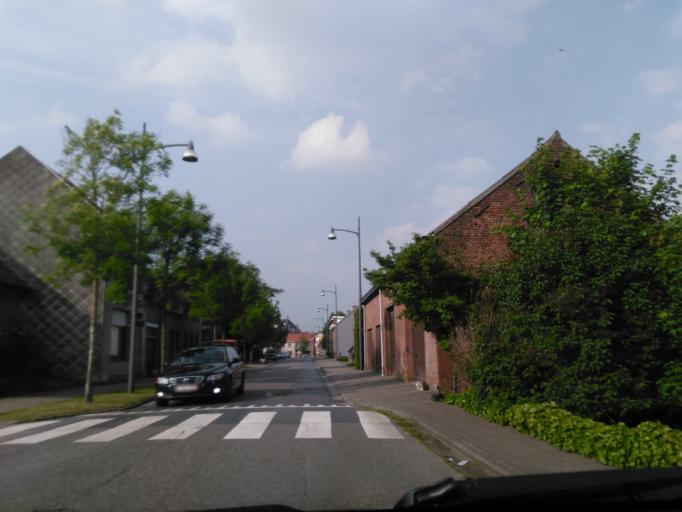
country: BE
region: Flanders
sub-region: Provincie Oost-Vlaanderen
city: Beveren
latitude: 51.2504
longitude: 4.2776
